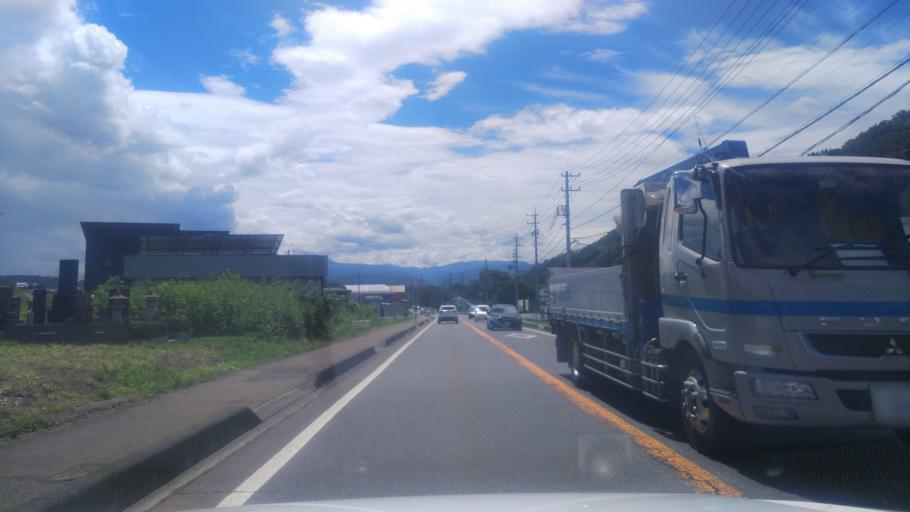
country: JP
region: Nagano
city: Ueda
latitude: 36.4340
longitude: 138.2989
